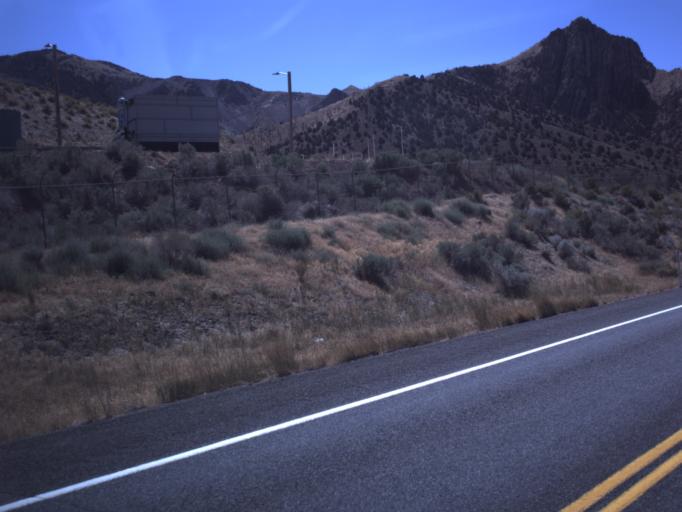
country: US
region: Utah
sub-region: Juab County
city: Nephi
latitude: 39.5630
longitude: -112.1998
